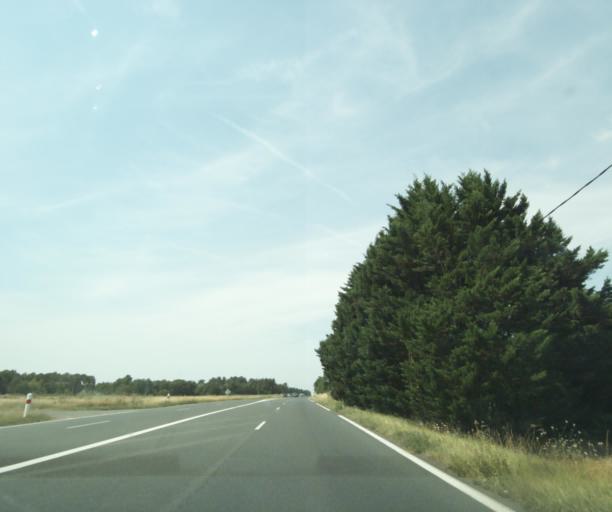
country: FR
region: Centre
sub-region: Departement d'Indre-et-Loire
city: La Celle-Saint-Avant
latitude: 47.0597
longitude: 0.6160
